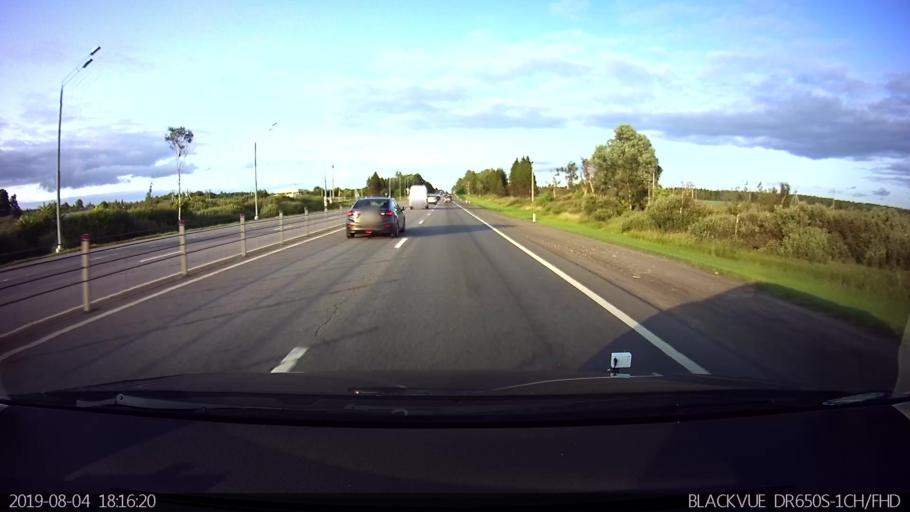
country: RU
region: Moskovskaya
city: Dorokhovo
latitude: 55.5099
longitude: 36.2476
